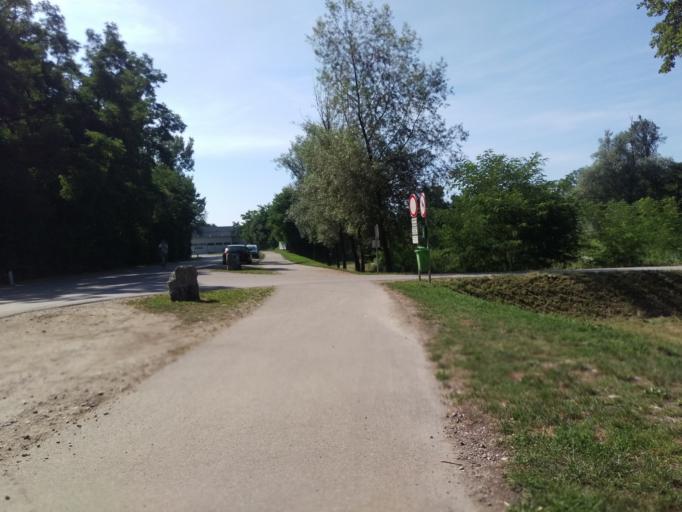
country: AT
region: Styria
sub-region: Politischer Bezirk Graz-Umgebung
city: Gossendorf
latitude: 46.9995
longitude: 15.4712
